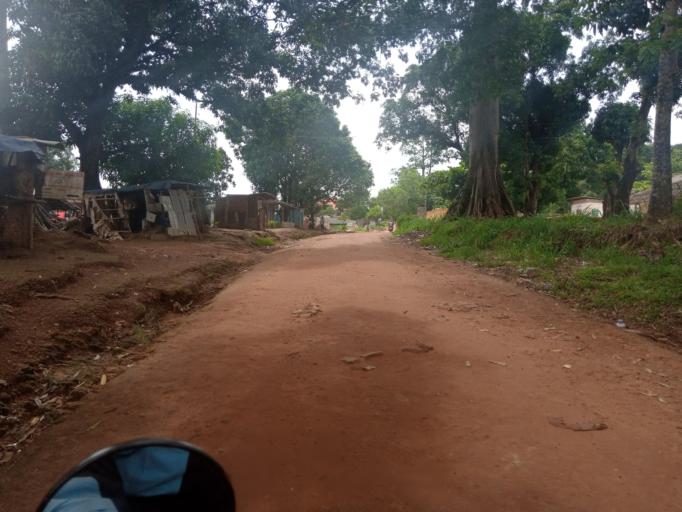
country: SL
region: Southern Province
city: Bo
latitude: 7.9641
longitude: -11.7470
